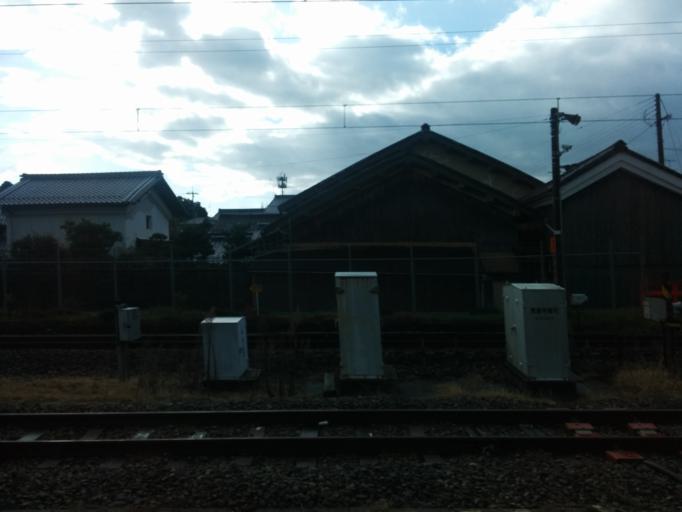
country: JP
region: Shiga Prefecture
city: Omihachiman
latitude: 35.1413
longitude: 136.1315
